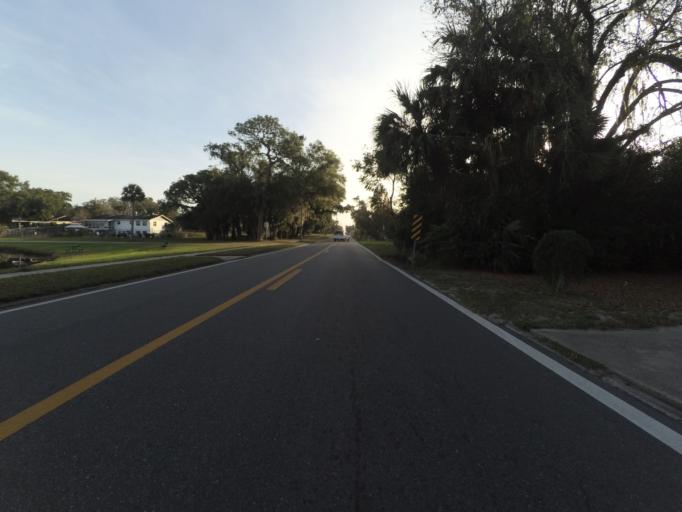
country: US
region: Florida
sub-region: Lake County
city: Umatilla
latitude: 28.9311
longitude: -81.6714
